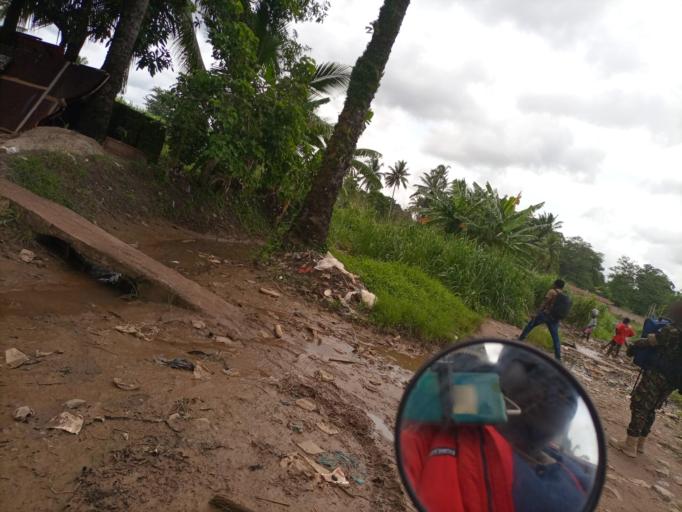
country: SL
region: Southern Province
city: Bo
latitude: 7.9508
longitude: -11.7444
